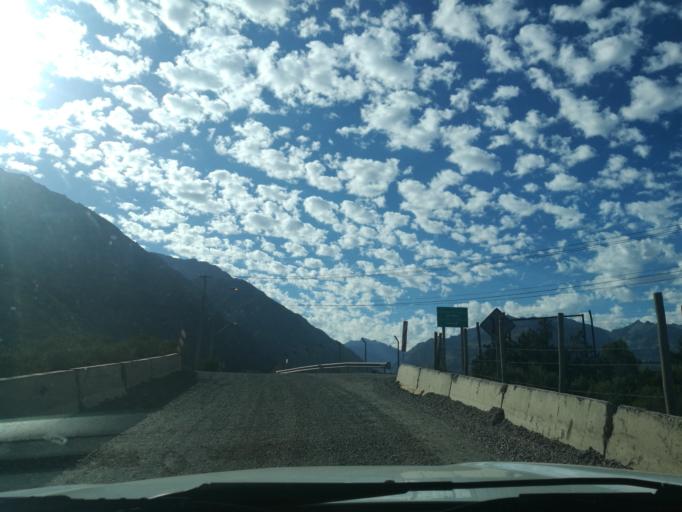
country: CL
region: O'Higgins
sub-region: Provincia de Cachapoal
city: Machali
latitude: -34.2943
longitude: -70.4329
